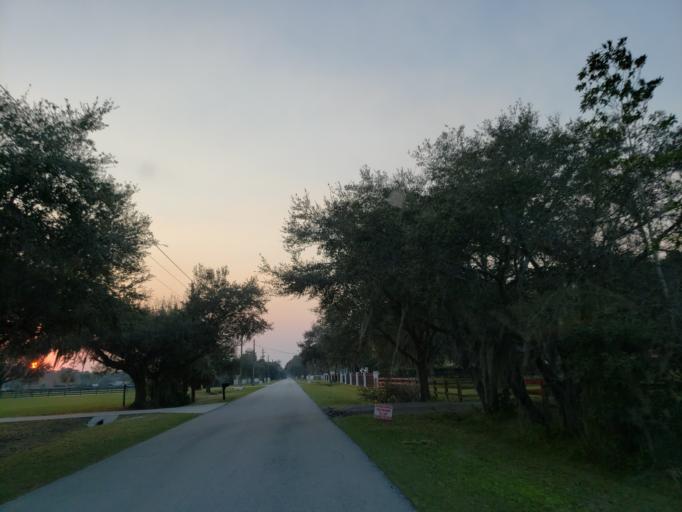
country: US
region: Florida
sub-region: Hillsborough County
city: Fish Hawk
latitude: 27.8427
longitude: -82.1796
